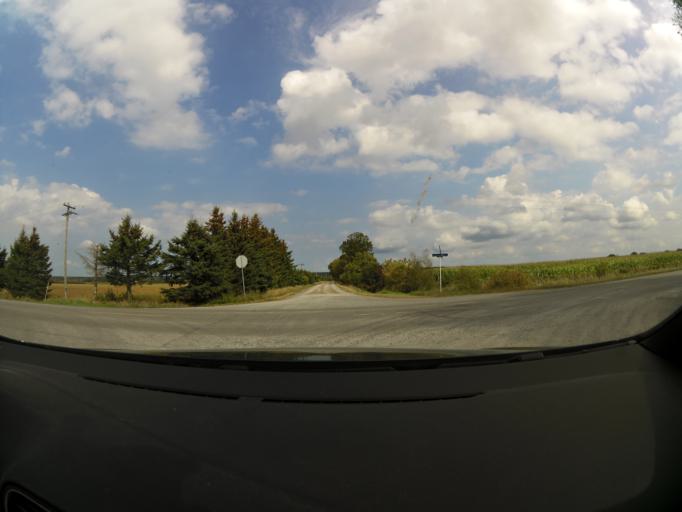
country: CA
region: Ontario
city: Arnprior
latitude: 45.3712
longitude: -76.1622
